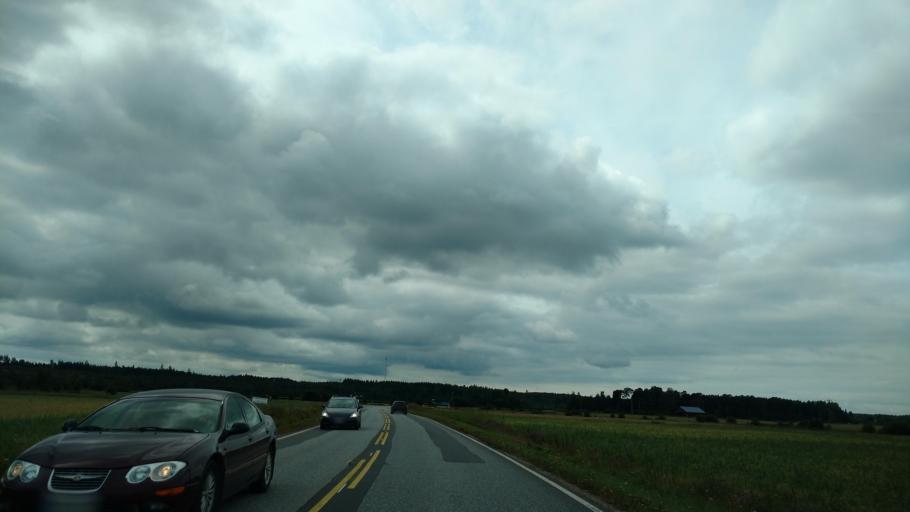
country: FI
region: Varsinais-Suomi
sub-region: Aboland-Turunmaa
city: Dragsfjaerd
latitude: 60.0988
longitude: 22.5518
